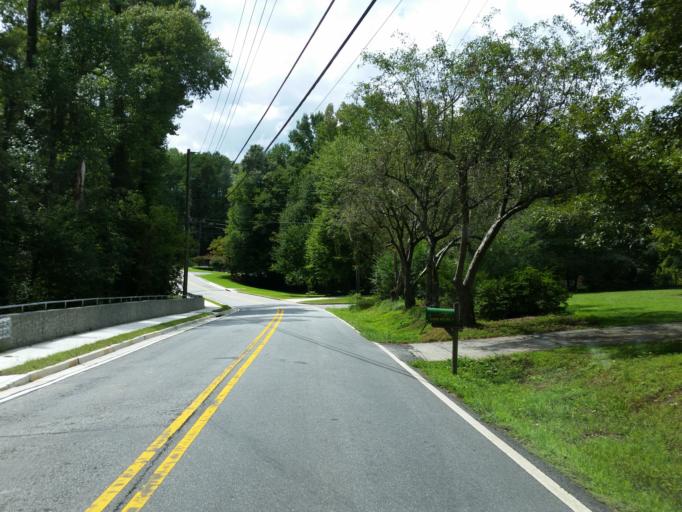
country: US
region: Georgia
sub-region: Cobb County
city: Marietta
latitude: 33.9527
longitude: -84.4736
